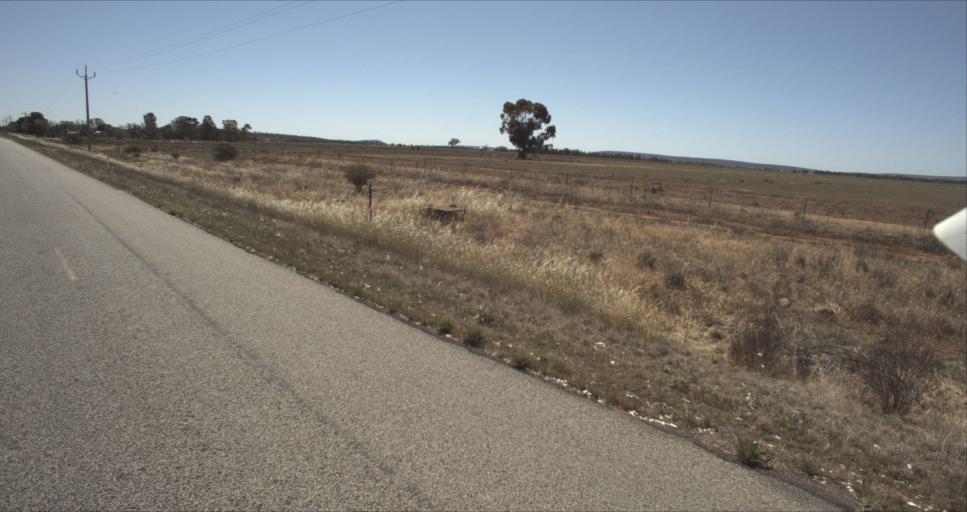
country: AU
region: New South Wales
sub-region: Leeton
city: Leeton
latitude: -34.4454
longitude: 146.2970
